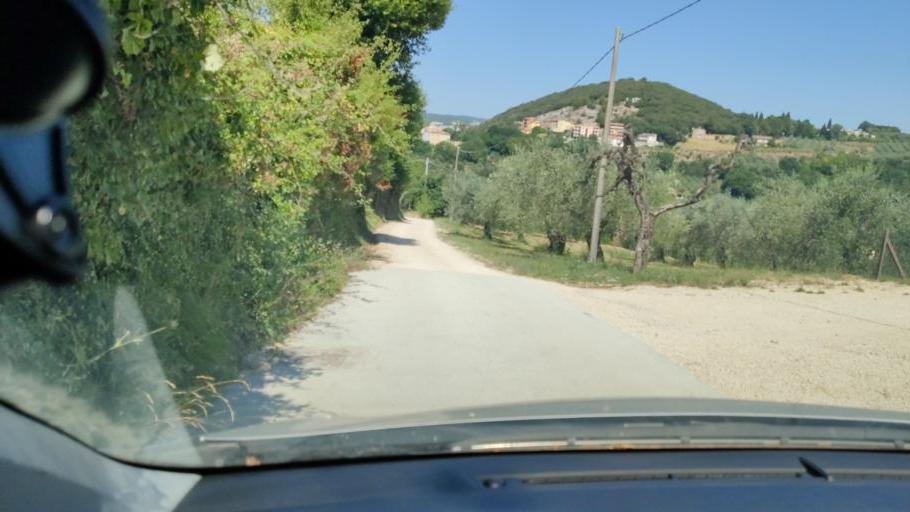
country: IT
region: Umbria
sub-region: Provincia di Terni
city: Amelia
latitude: 42.5457
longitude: 12.4331
